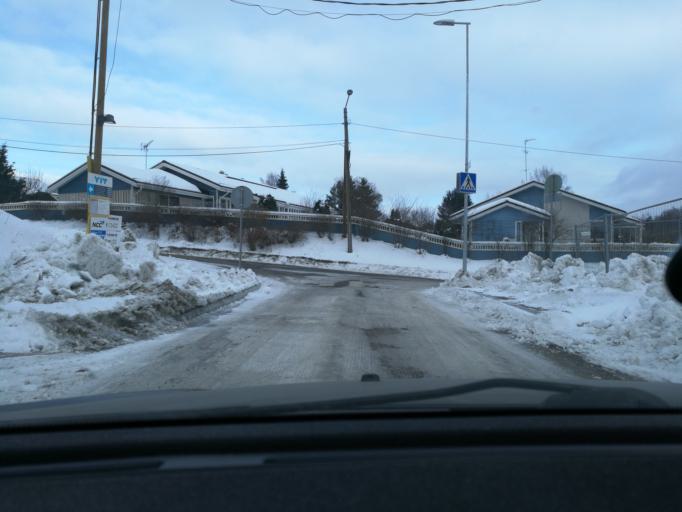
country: FI
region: Uusimaa
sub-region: Helsinki
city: Vantaa
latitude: 60.2825
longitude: 25.0980
